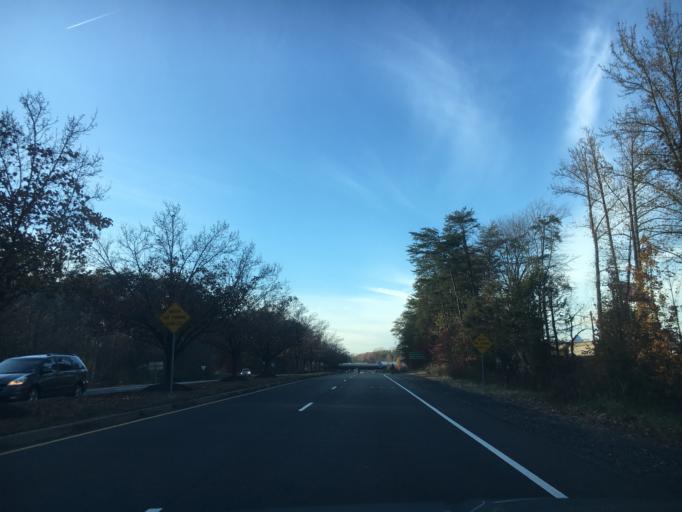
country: US
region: Virginia
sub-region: Prince William County
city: Triangle
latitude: 38.5477
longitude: -77.3398
